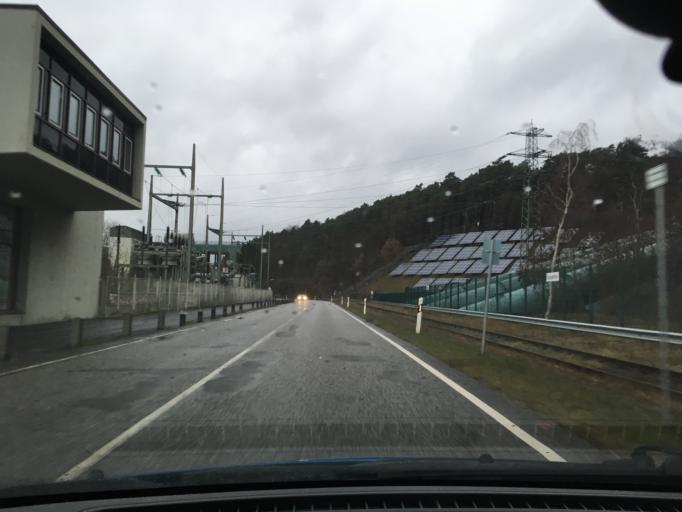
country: DE
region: Lower Saxony
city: Marschacht
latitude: 53.4187
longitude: 10.3950
